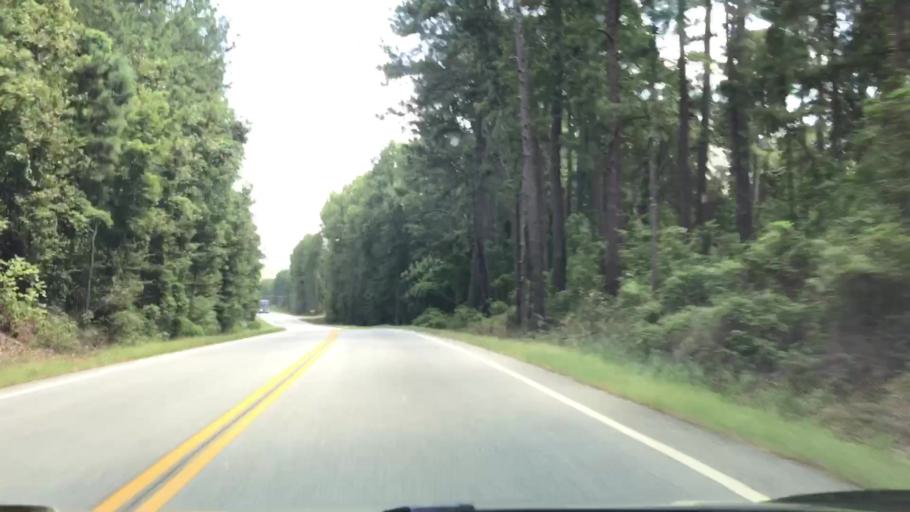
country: US
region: Georgia
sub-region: Greene County
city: Greensboro
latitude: 33.6807
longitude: -83.2716
